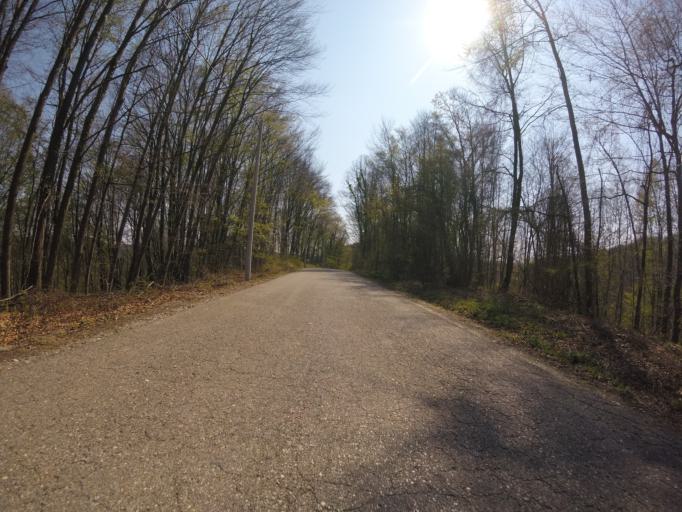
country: HR
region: Grad Zagreb
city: Strmec
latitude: 45.6215
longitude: 15.9511
